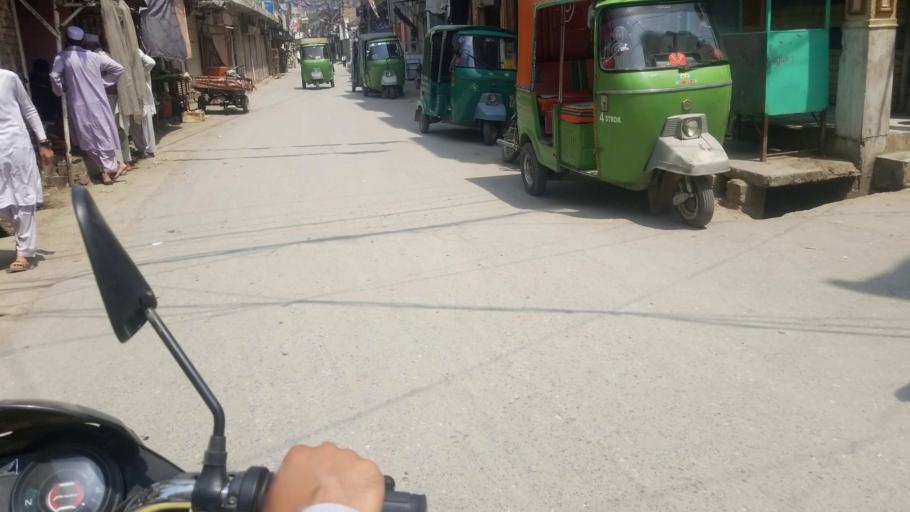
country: PK
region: Khyber Pakhtunkhwa
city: Peshawar
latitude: 34.0287
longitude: 71.5885
